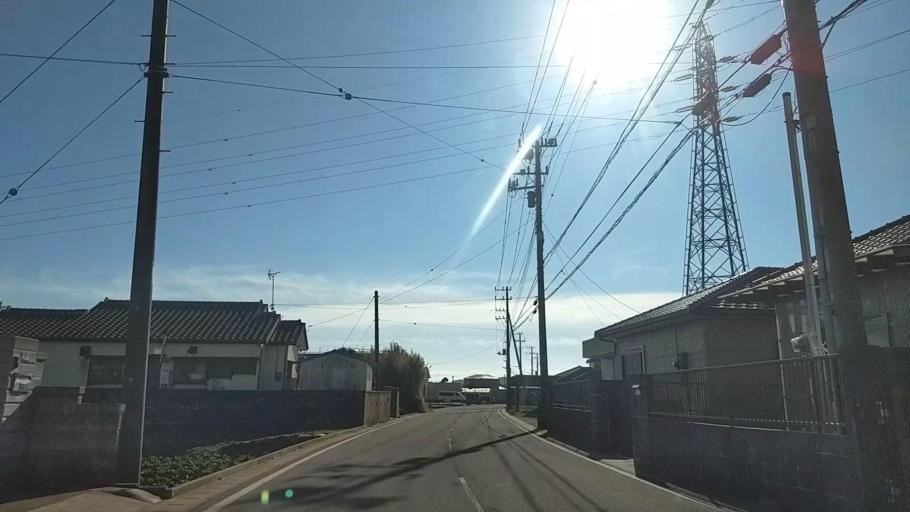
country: JP
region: Chiba
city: Hasaki
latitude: 35.7221
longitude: 140.8437
